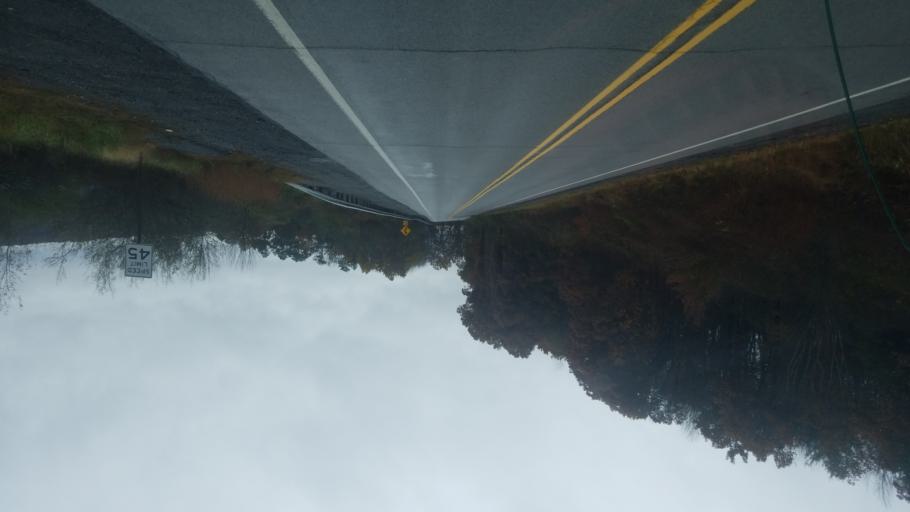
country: US
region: Pennsylvania
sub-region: Clearfield County
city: Clearfield
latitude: 41.0430
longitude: -78.3928
